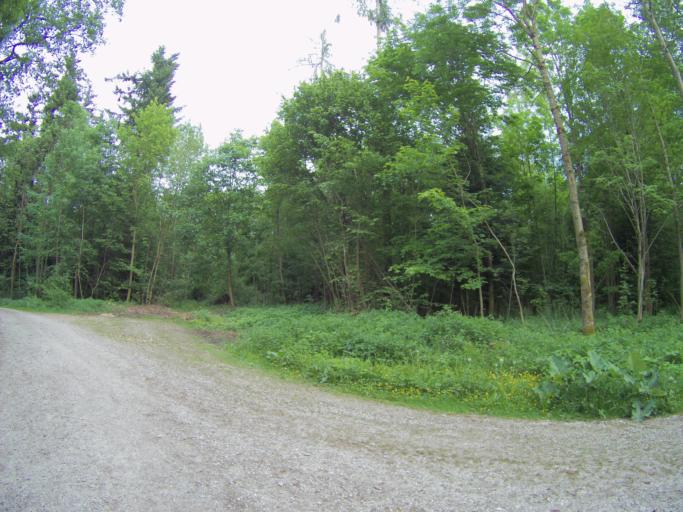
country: DE
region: Bavaria
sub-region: Upper Bavaria
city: Freising
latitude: 48.4197
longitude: 11.7352
